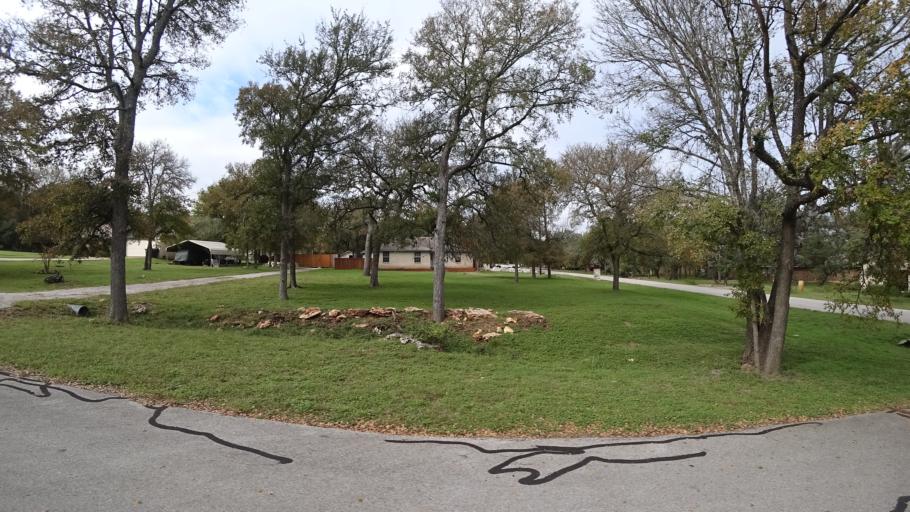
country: US
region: Texas
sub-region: Travis County
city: Shady Hollow
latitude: 30.1387
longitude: -97.8857
